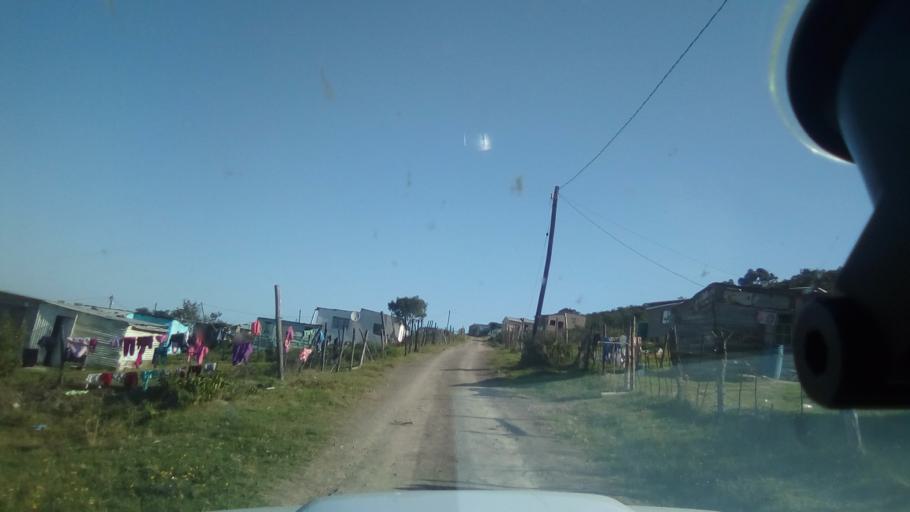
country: ZA
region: Eastern Cape
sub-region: Buffalo City Metropolitan Municipality
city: Bhisho
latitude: -32.8118
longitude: 27.3518
